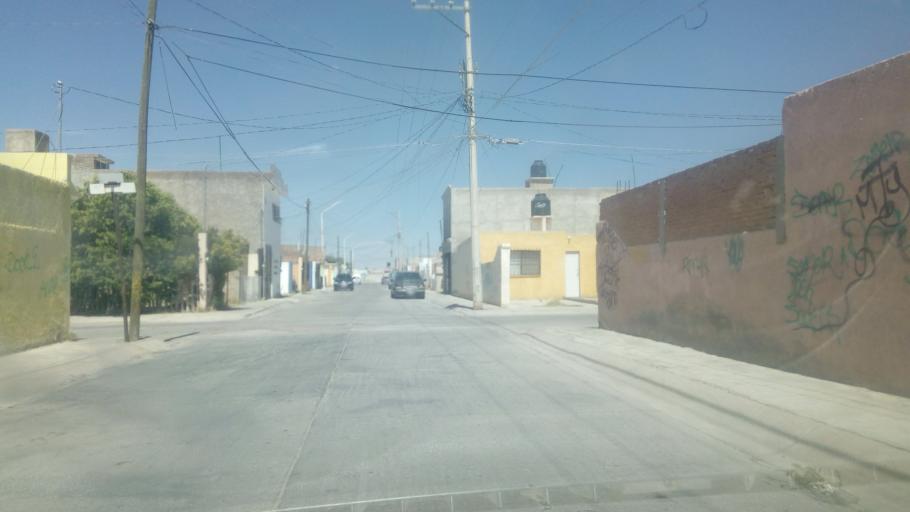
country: MX
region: Durango
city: Victoria de Durango
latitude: 24.0045
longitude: -104.6263
